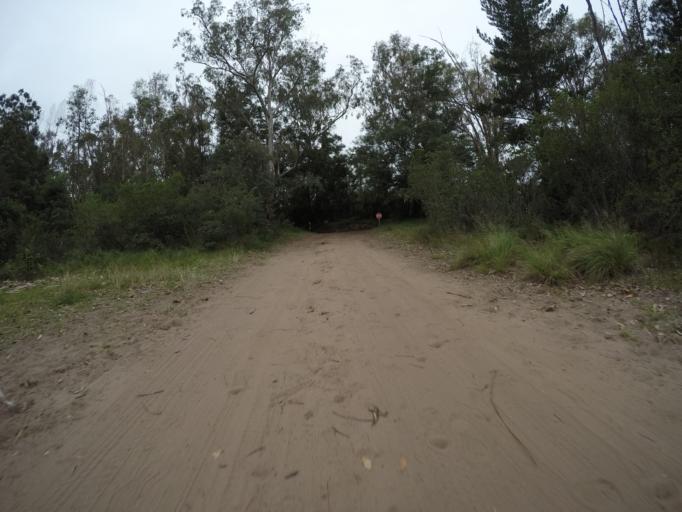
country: ZA
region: Western Cape
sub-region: Eden District Municipality
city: Knysna
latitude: -34.0056
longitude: 22.7947
